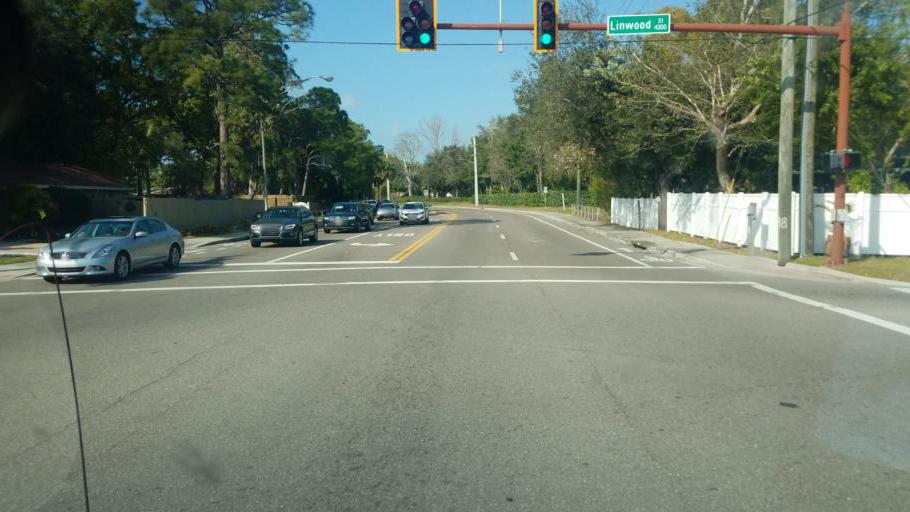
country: US
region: Florida
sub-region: Sarasota County
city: Sarasota Springs
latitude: 27.3151
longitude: -82.4822
